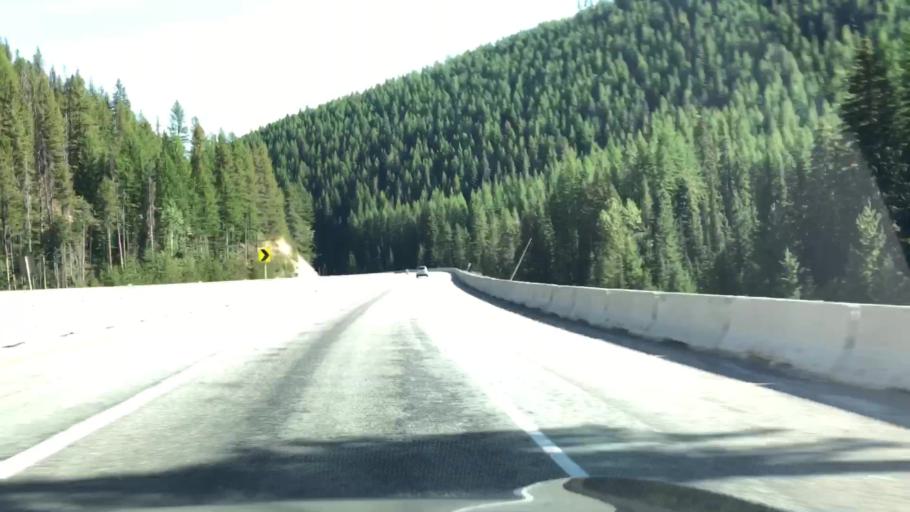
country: US
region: Idaho
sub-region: Shoshone County
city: Wallace
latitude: 47.4348
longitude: -115.6546
